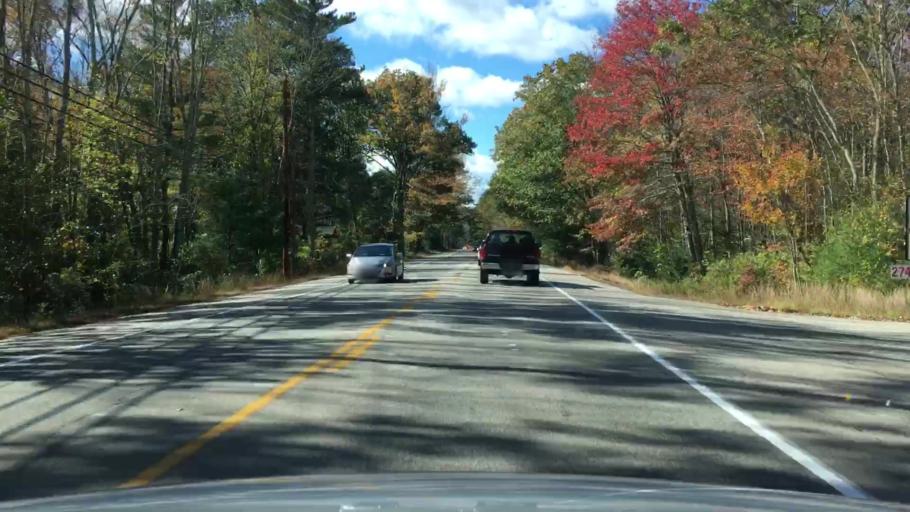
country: US
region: Maine
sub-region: York County
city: Alfred
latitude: 43.4763
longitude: -70.6836
